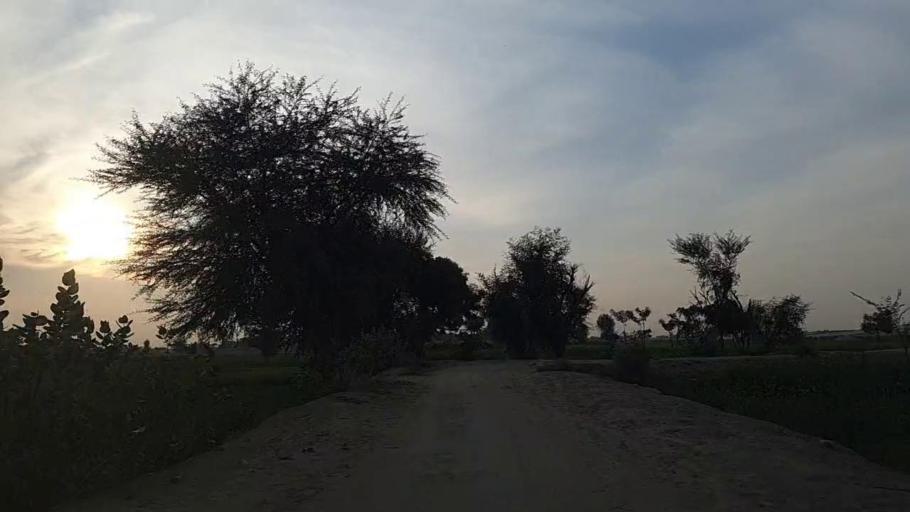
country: PK
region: Sindh
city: Jam Sahib
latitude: 26.4650
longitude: 68.5627
